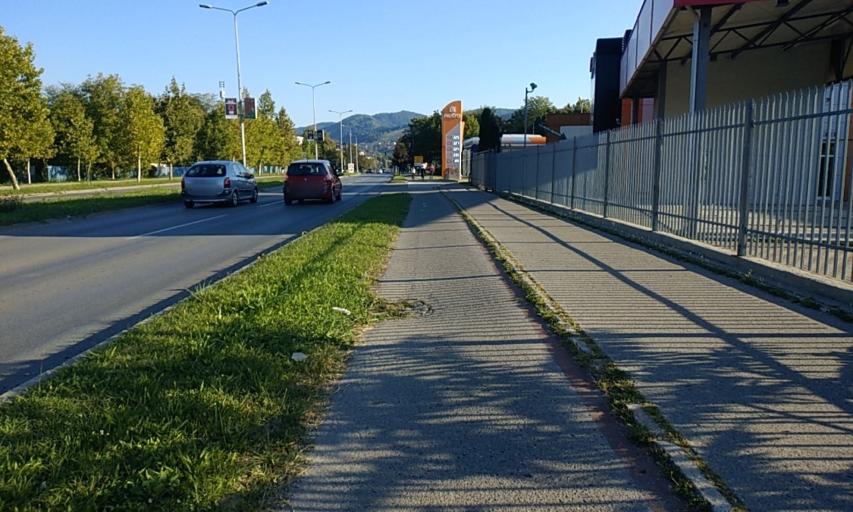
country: BA
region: Republika Srpska
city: Starcevica
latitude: 44.7765
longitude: 17.2066
